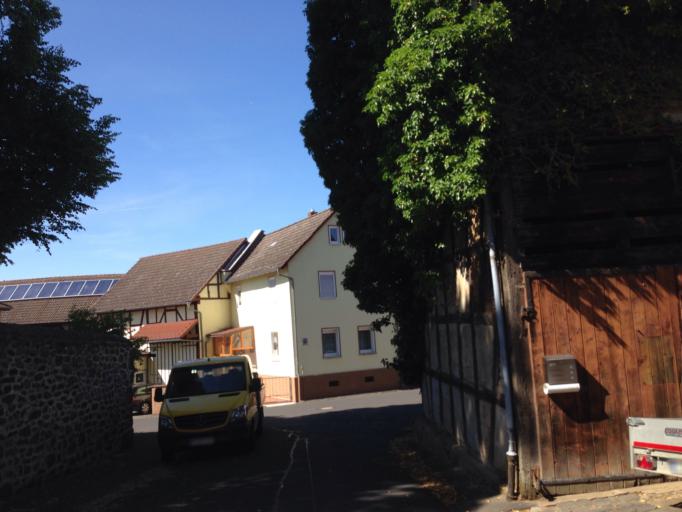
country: DE
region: Hesse
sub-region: Regierungsbezirk Giessen
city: Alten Buseck
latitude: 50.6000
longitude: 8.7504
